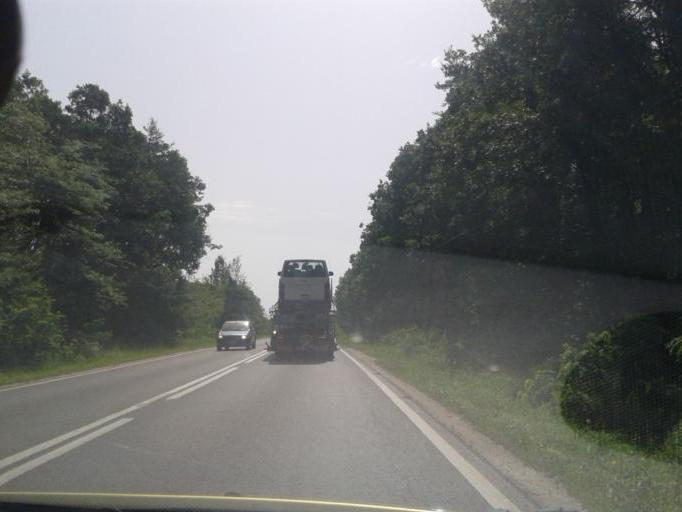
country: RO
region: Arges
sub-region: Comuna Cotmeana
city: Cotmeana
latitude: 44.9897
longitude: 24.6387
